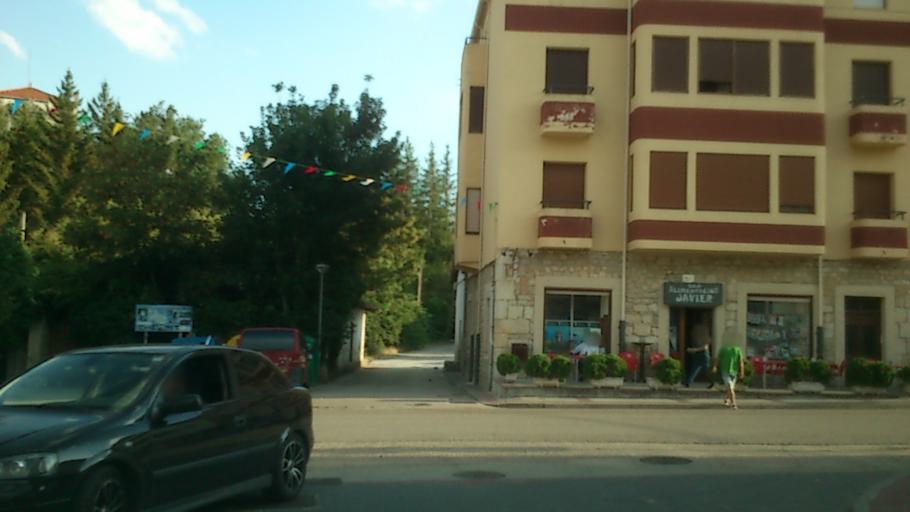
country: ES
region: Castille and Leon
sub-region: Provincia de Burgos
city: Frias
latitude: 42.7928
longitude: -3.2701
